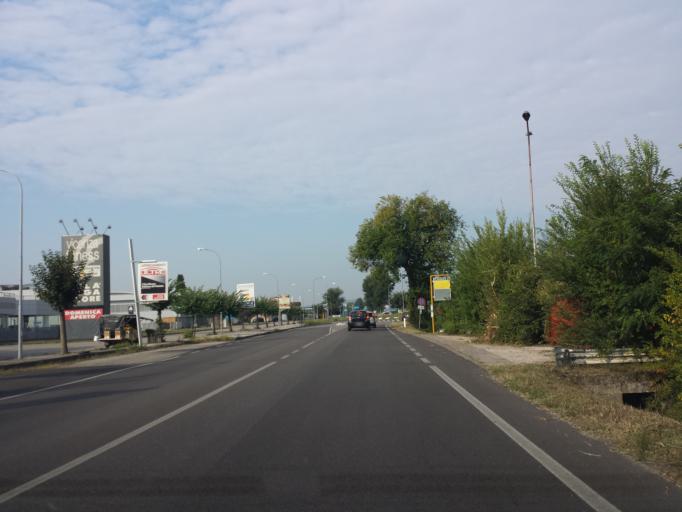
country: IT
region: Veneto
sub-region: Provincia di Vicenza
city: Creazzo
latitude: 45.5212
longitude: 11.4806
